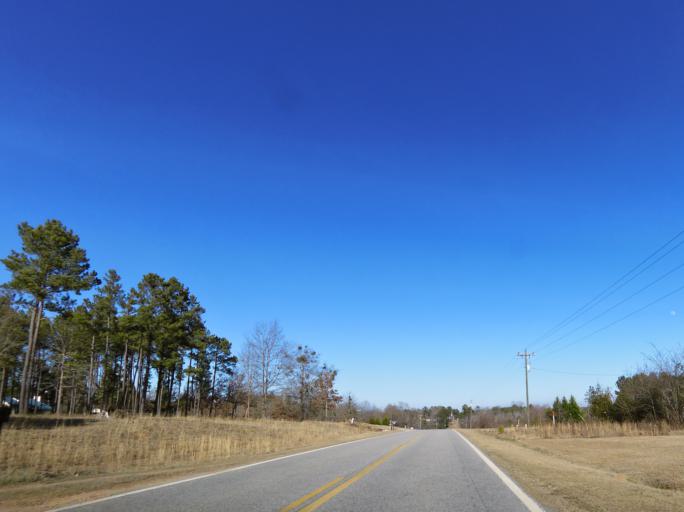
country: US
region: Georgia
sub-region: Bibb County
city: West Point
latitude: 32.7590
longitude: -83.8811
